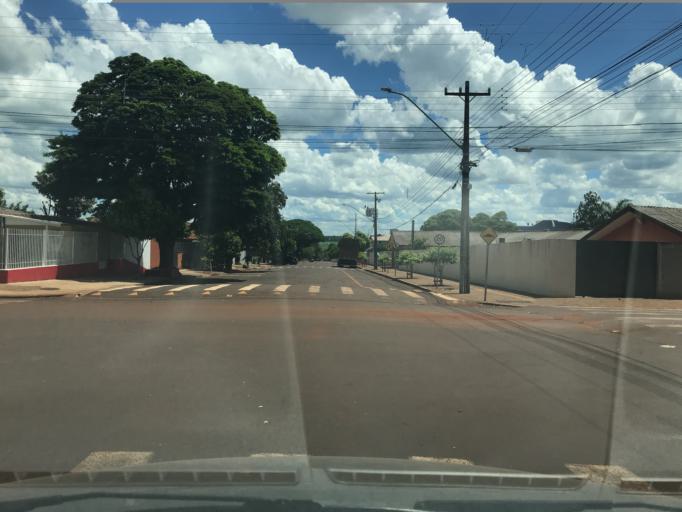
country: BR
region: Parana
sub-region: Palotina
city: Palotina
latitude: -24.2793
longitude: -53.8424
